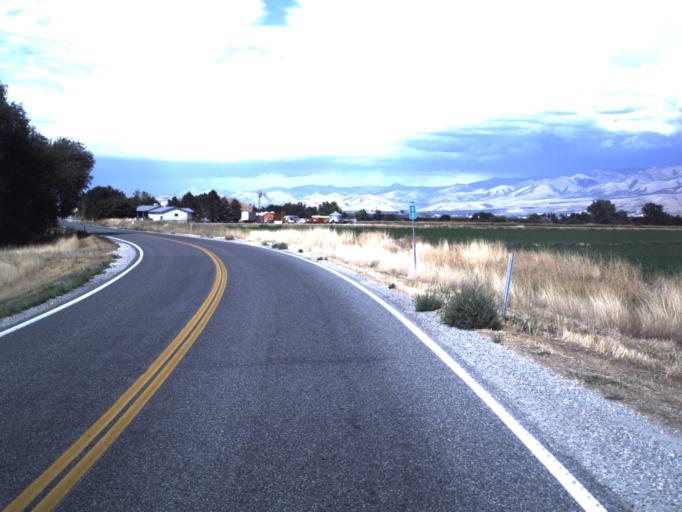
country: US
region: Utah
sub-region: Cache County
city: Lewiston
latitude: 41.9155
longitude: -111.9119
